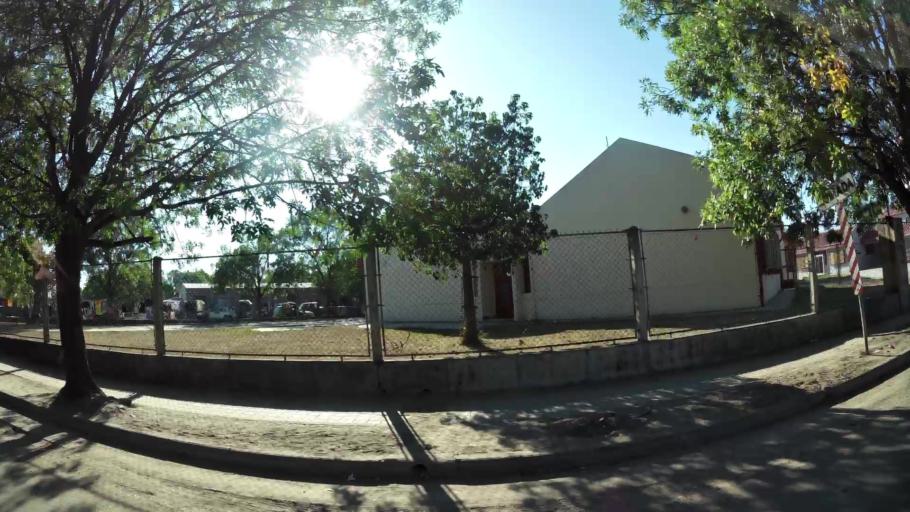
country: AR
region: Cordoba
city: Villa Allende
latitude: -31.3361
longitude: -64.2465
